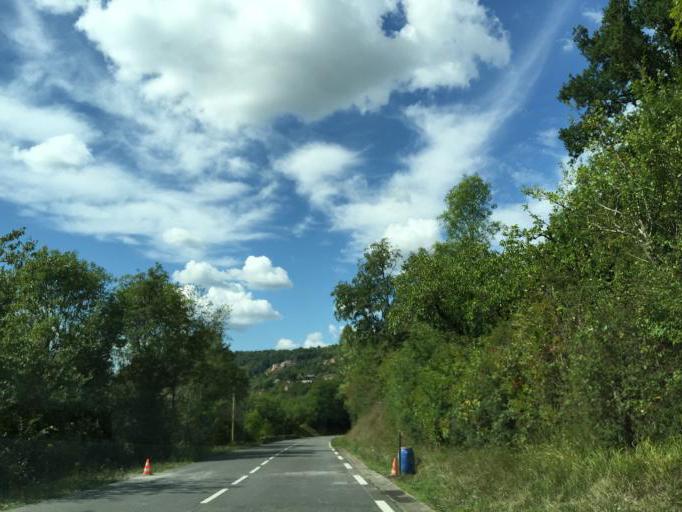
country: FR
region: Midi-Pyrenees
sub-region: Departement de l'Aveyron
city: Salles-la-Source
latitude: 44.4399
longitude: 2.5021
